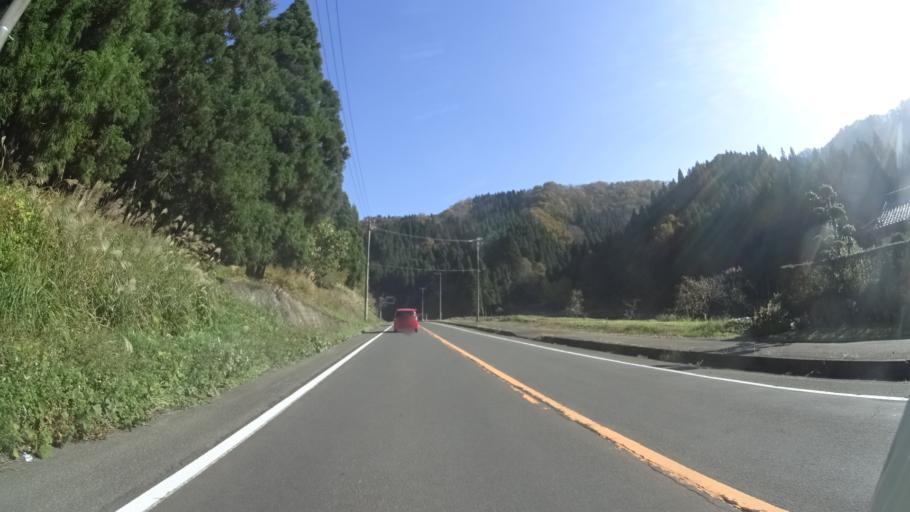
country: JP
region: Fukui
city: Ono
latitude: 35.9925
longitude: 136.4489
